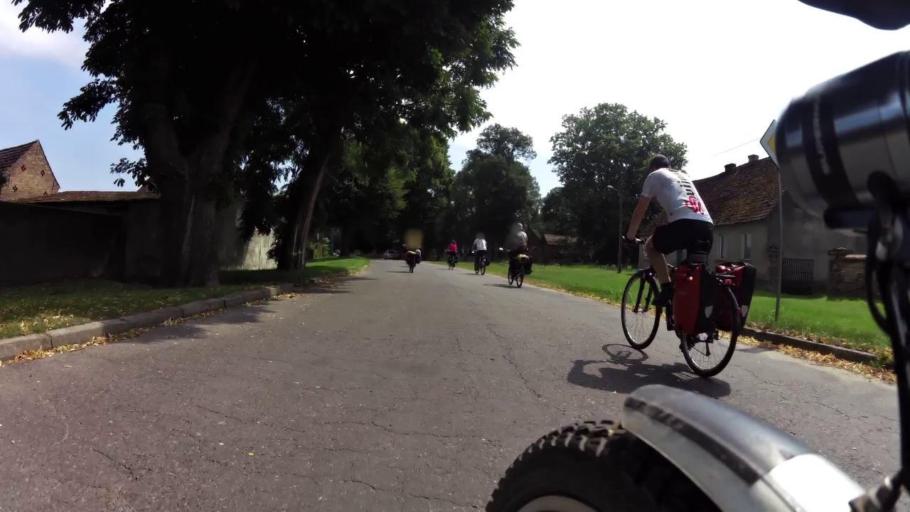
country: PL
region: West Pomeranian Voivodeship
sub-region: Powiat mysliborski
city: Boleszkowice
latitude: 52.6781
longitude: 14.6162
